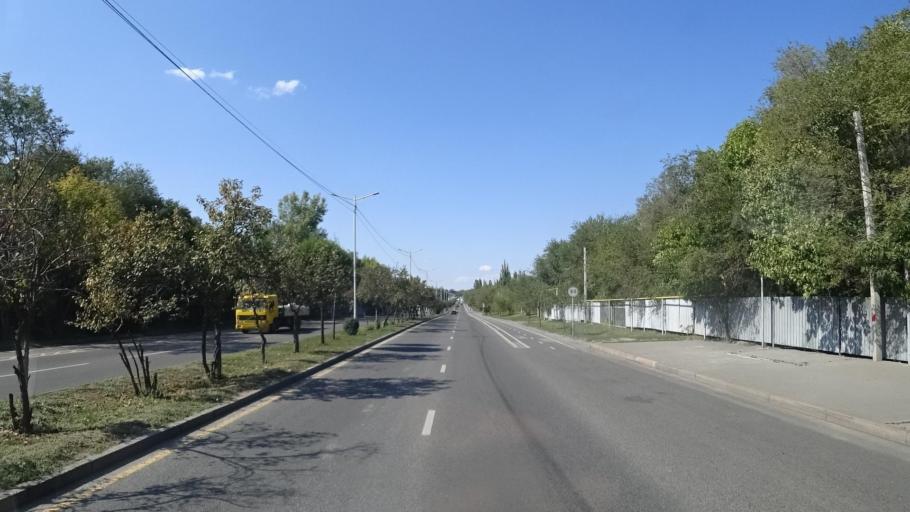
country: KZ
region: Almaty Oblysy
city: Pervomayskiy
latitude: 43.3380
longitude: 77.0006
